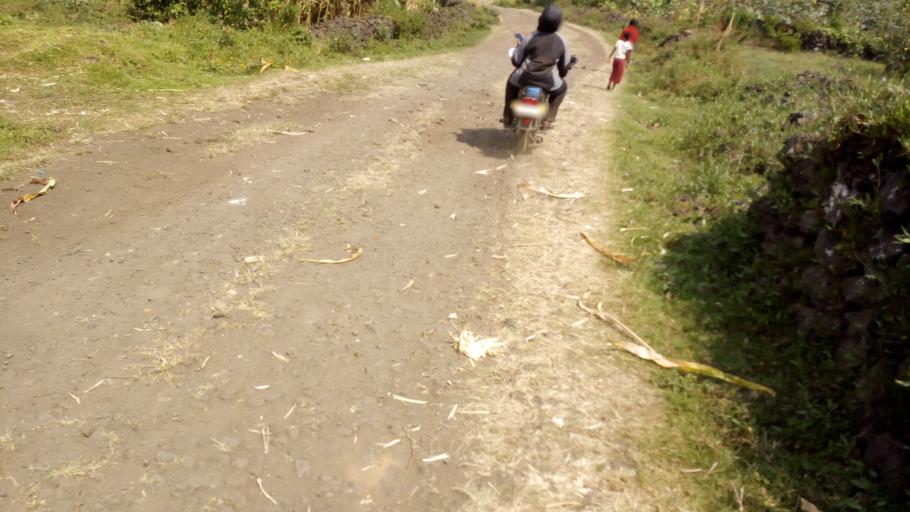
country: UG
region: Western Region
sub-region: Kisoro District
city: Kisoro
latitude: -1.3347
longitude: 29.7630
